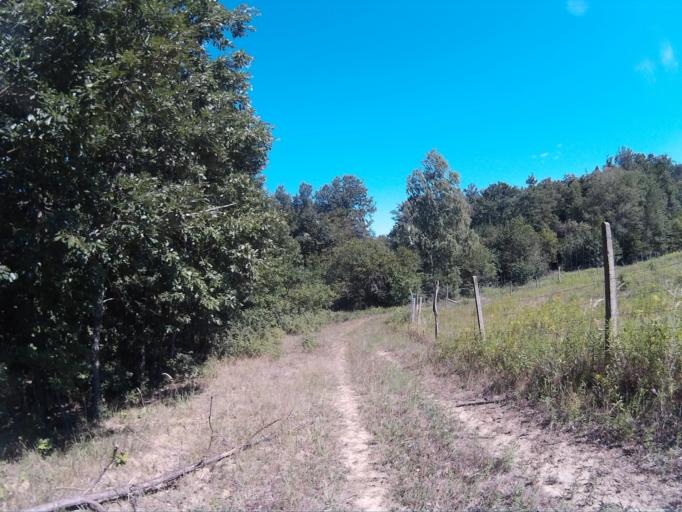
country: HU
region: Zala
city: Zalalovo
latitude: 46.8025
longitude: 16.6572
